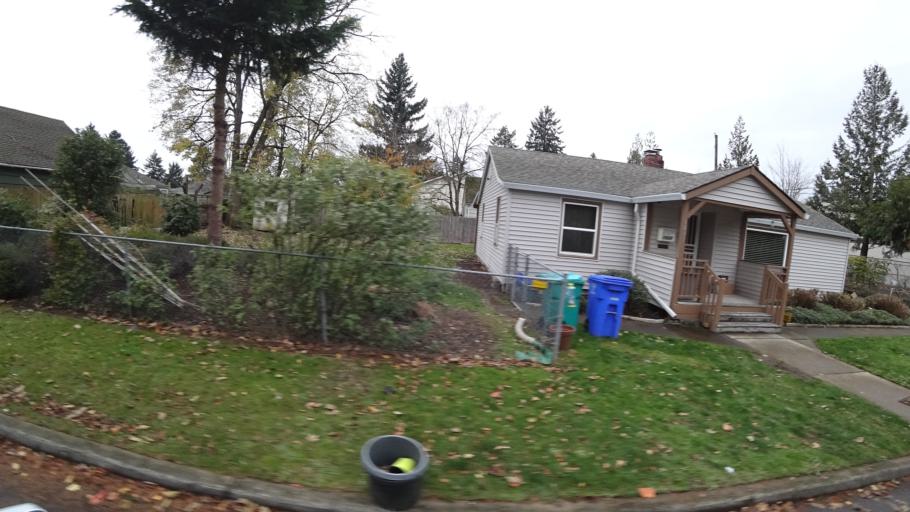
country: US
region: Oregon
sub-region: Multnomah County
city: Lents
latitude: 45.5304
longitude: -122.5556
